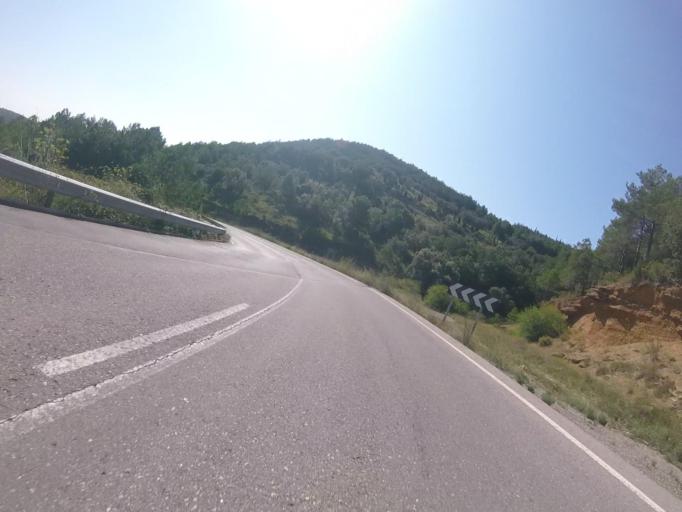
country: ES
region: Valencia
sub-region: Provincia de Castello
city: Benafigos
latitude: 40.2674
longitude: -0.2439
